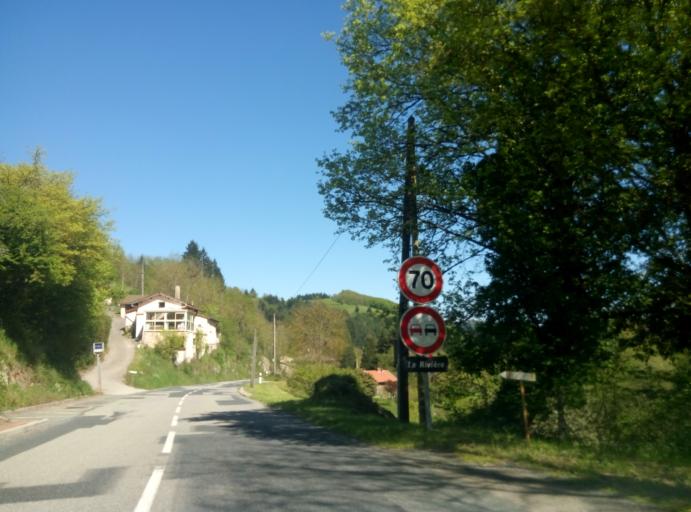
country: FR
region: Rhone-Alpes
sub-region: Departement du Rhone
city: Grandris
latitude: 46.0044
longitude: 4.4694
